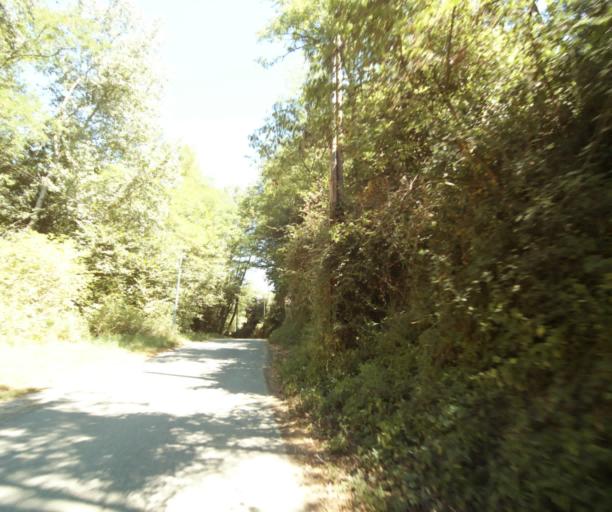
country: FR
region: Midi-Pyrenees
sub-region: Departement de la Haute-Garonne
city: Castanet-Tolosan
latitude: 43.5067
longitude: 1.4939
